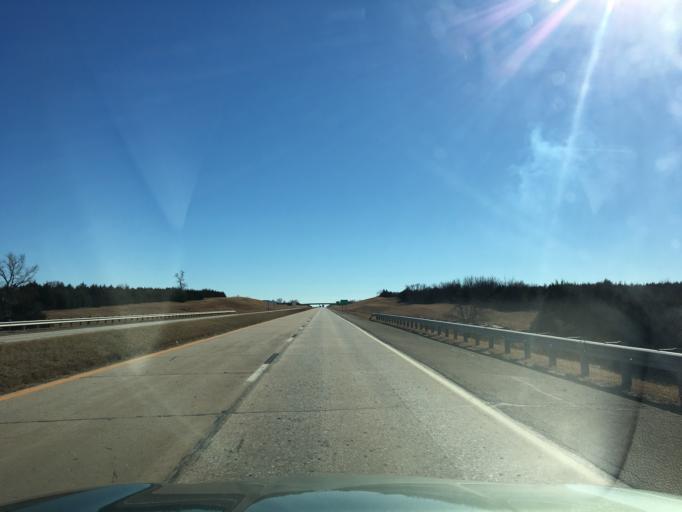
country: US
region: Oklahoma
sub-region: Pawnee County
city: Pawnee
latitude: 36.2867
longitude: -96.9828
